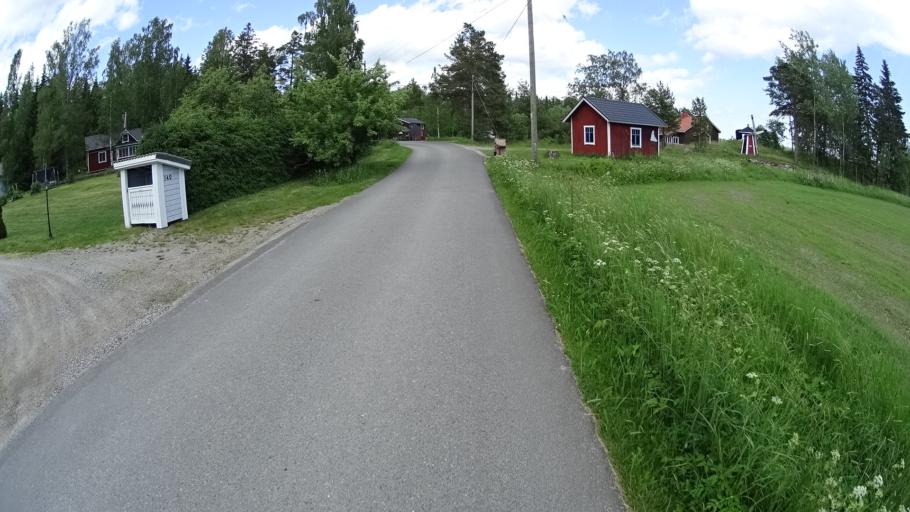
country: FI
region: Uusimaa
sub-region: Helsinki
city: Sibbo
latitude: 60.2597
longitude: 25.3202
